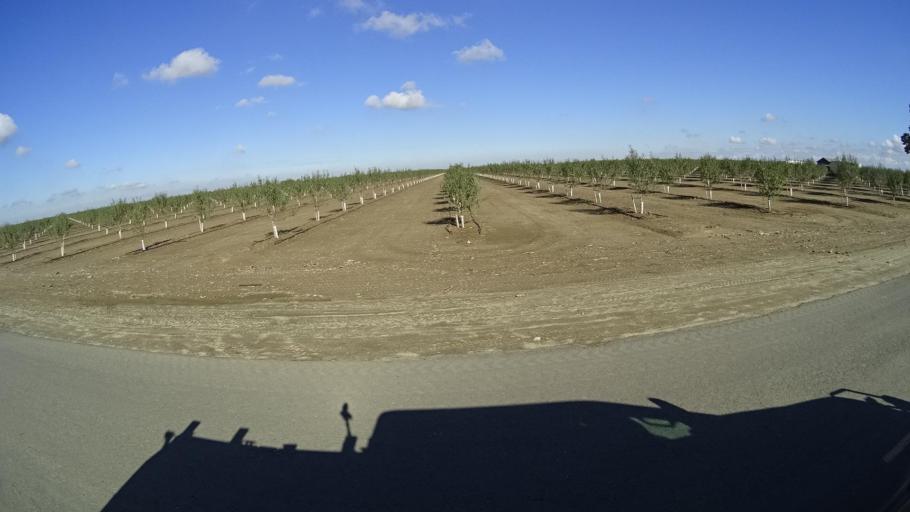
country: US
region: California
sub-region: Kern County
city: McFarland
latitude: 35.6597
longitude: -119.2517
